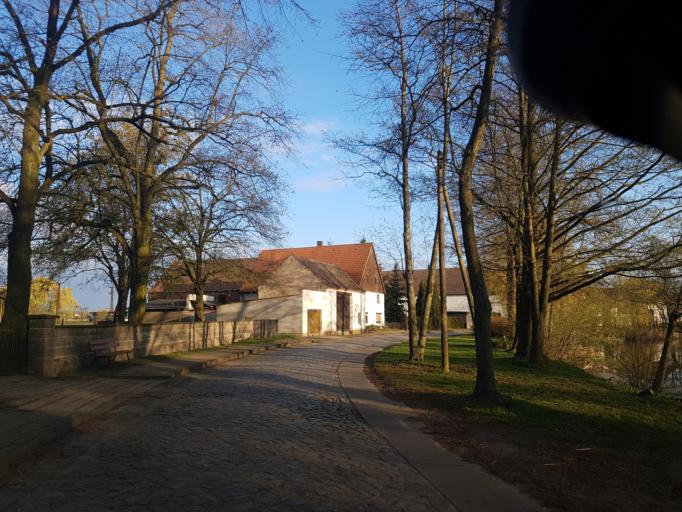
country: DE
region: Brandenburg
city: Juterbog
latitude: 51.9263
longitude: 13.1390
